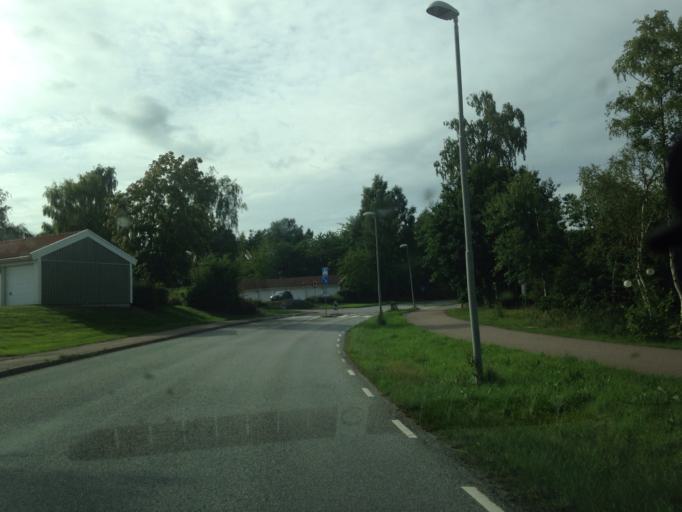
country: SE
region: Vaestra Goetaland
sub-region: Goteborg
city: Goeteborg
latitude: 57.7584
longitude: 11.9665
